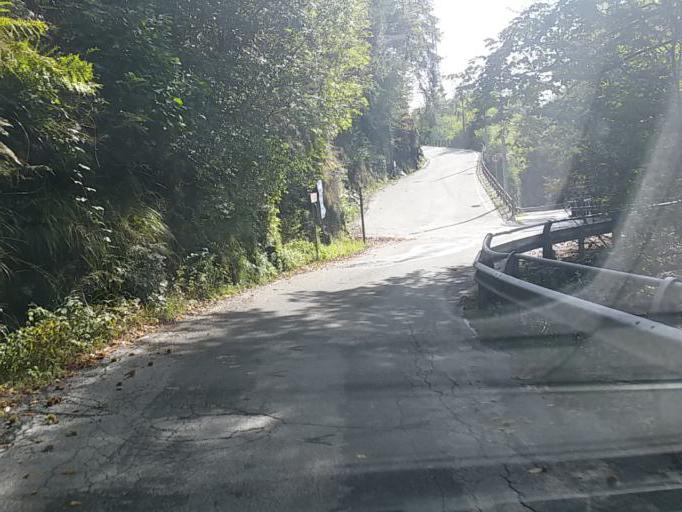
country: IT
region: Piedmont
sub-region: Provincia Verbano-Cusio-Ossola
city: Cursolo
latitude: 46.0958
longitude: 8.5822
